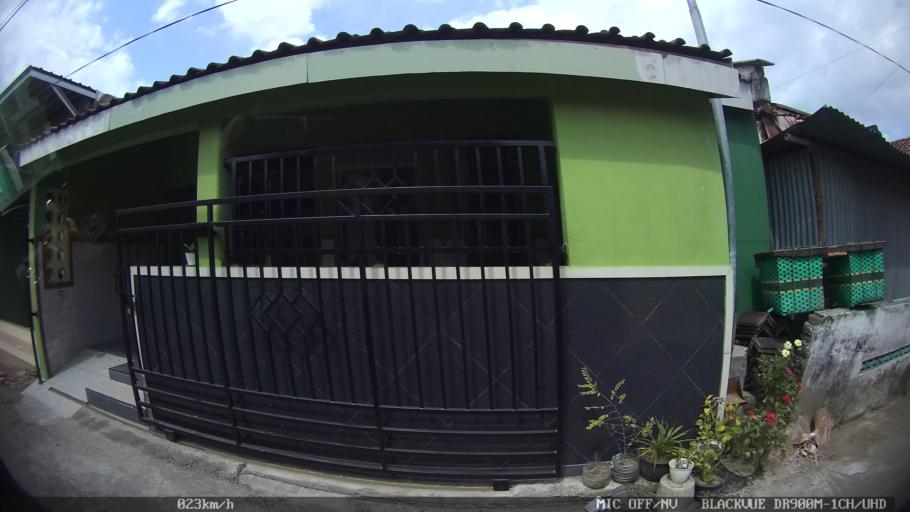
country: ID
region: Daerah Istimewa Yogyakarta
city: Gamping Lor
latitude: -7.8068
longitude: 110.3372
